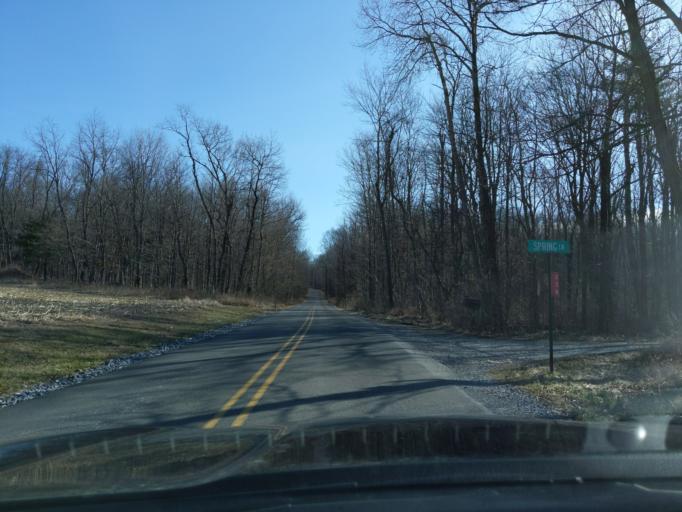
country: US
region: Pennsylvania
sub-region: Blair County
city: Martinsburg
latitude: 40.3740
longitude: -78.2723
